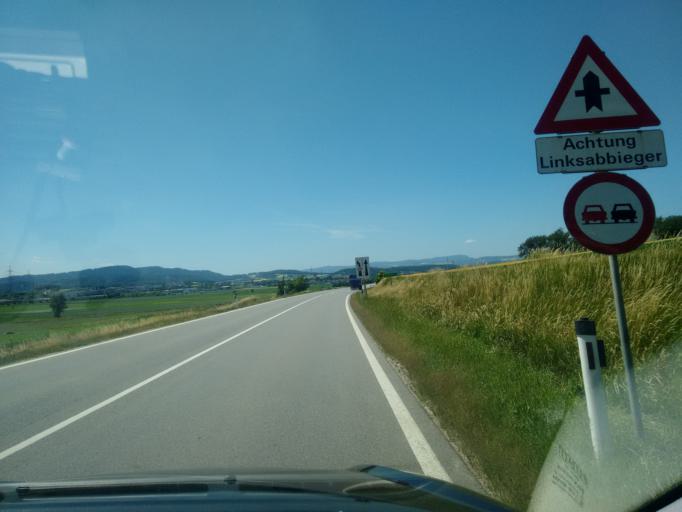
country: AT
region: Lower Austria
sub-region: Politischer Bezirk Sankt Polten
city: Haunoldstein
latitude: 48.1926
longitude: 15.4337
